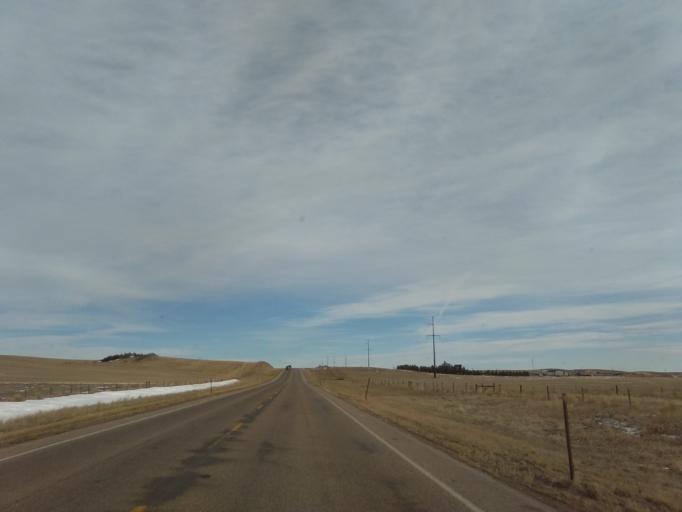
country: US
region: Wyoming
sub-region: Laramie County
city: Ranchettes
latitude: 41.3780
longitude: -104.5364
